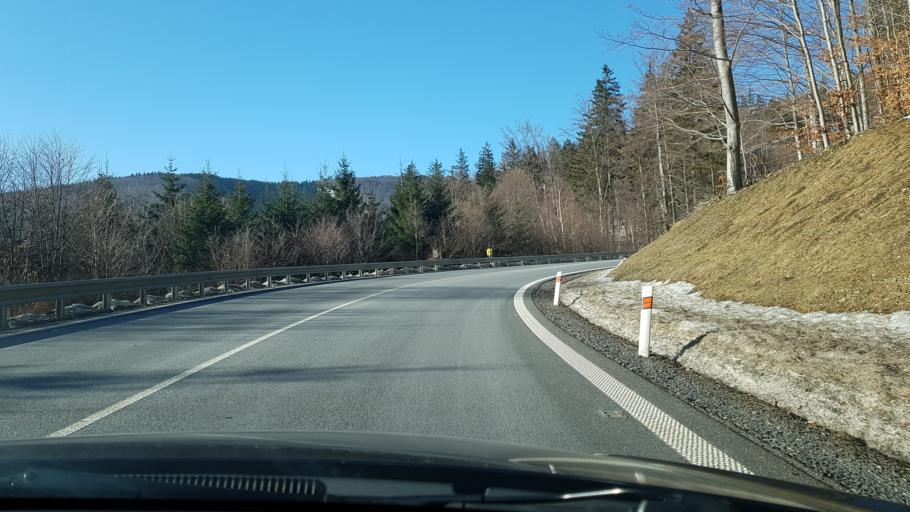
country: CZ
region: Olomoucky
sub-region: Okres Sumperk
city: Loucna nad Desnou
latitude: 50.1075
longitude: 17.1450
